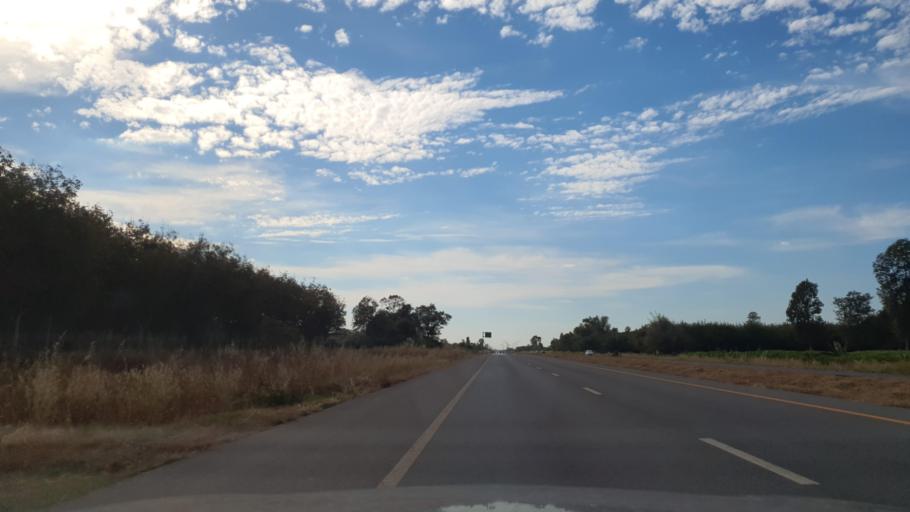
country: TH
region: Roi Et
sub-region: Amphoe Pho Chai
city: Pho Chai
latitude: 16.4156
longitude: 103.8170
